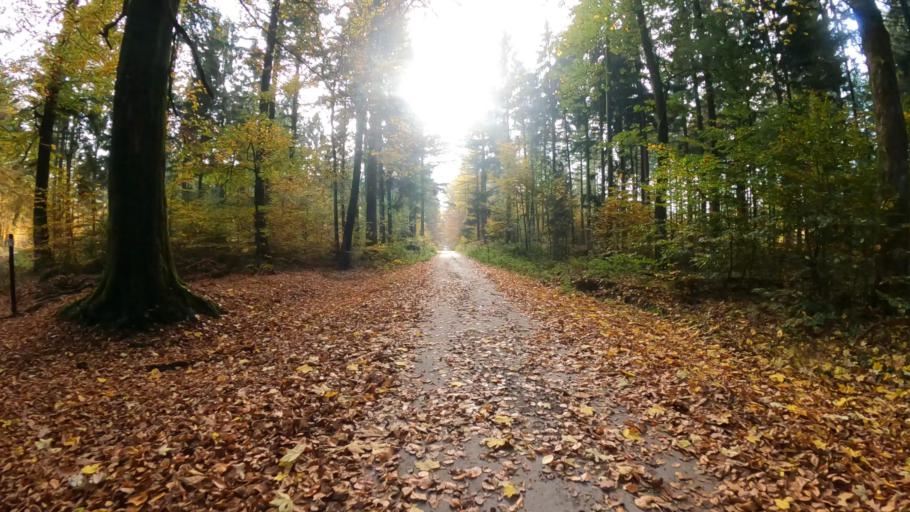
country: DE
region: Lower Saxony
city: Neu Wulmstorf
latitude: 53.3969
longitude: 9.8345
